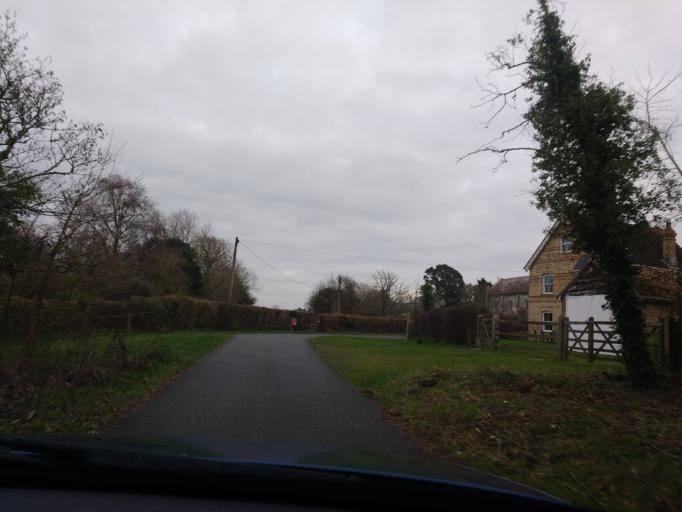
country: GB
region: England
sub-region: Isle of Wight
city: Shalfleet
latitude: 50.7149
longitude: -1.4049
